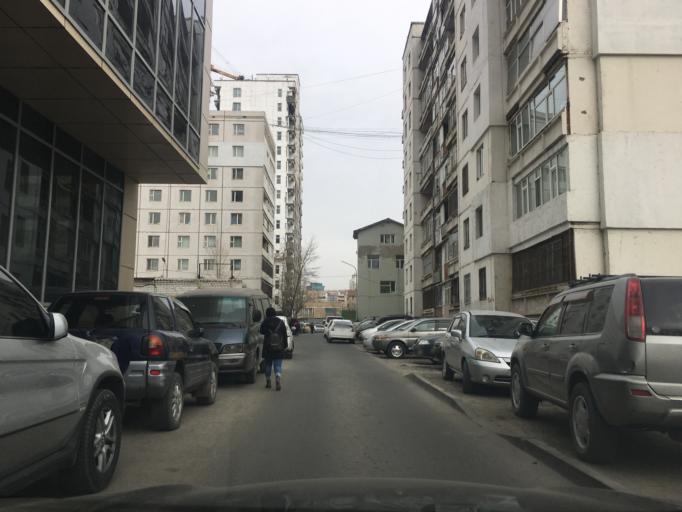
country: MN
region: Ulaanbaatar
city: Ulaanbaatar
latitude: 47.9098
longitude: 106.8893
